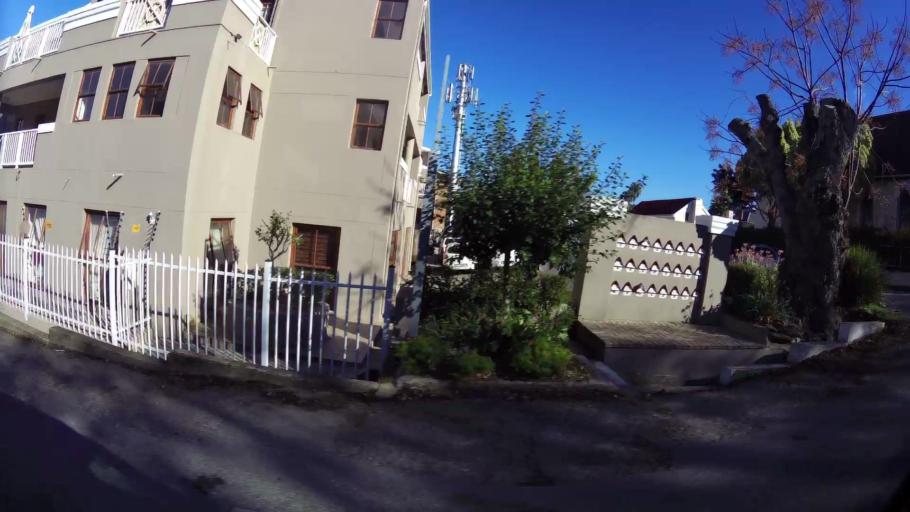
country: ZA
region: Western Cape
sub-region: Eden District Municipality
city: Knysna
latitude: -34.0351
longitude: 23.0522
